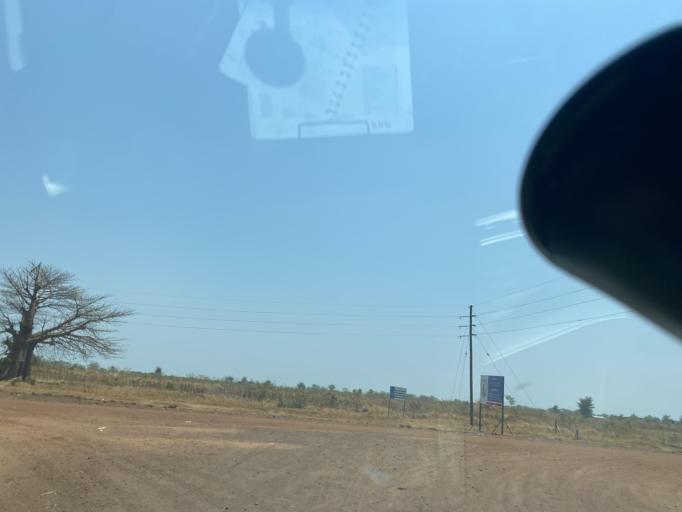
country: ZM
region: Southern
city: Nakambala
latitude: -15.4734
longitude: 27.8968
